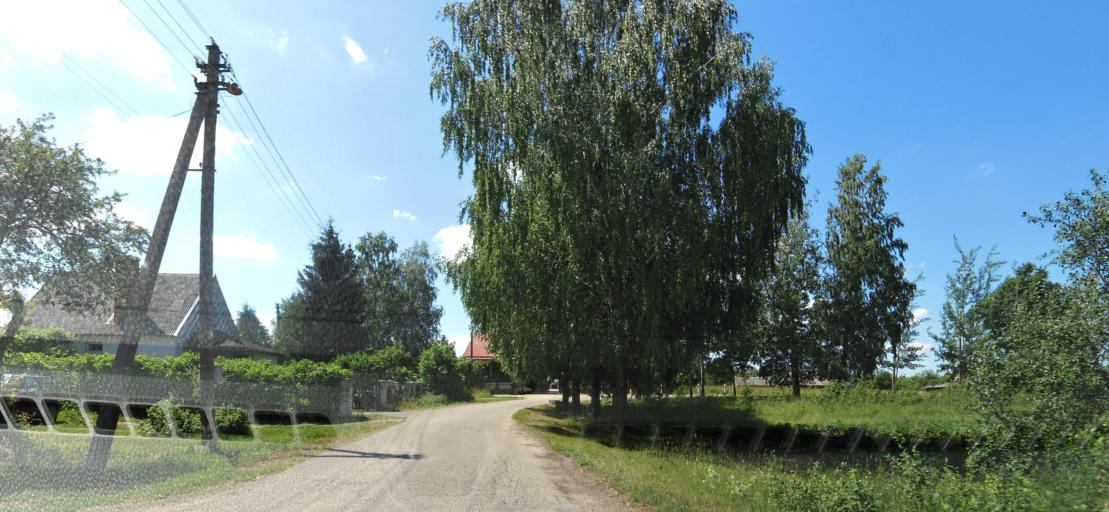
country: LT
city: Nemencine
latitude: 54.8693
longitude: 25.3570
